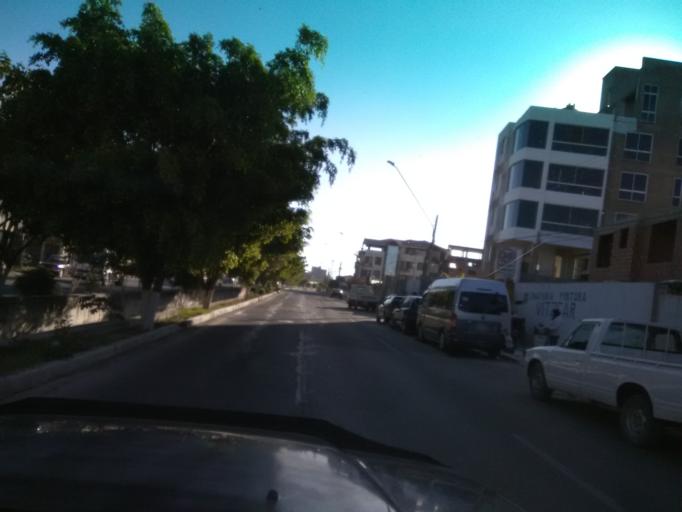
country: BO
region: Cochabamba
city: Cochabamba
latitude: -17.3826
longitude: -66.1880
